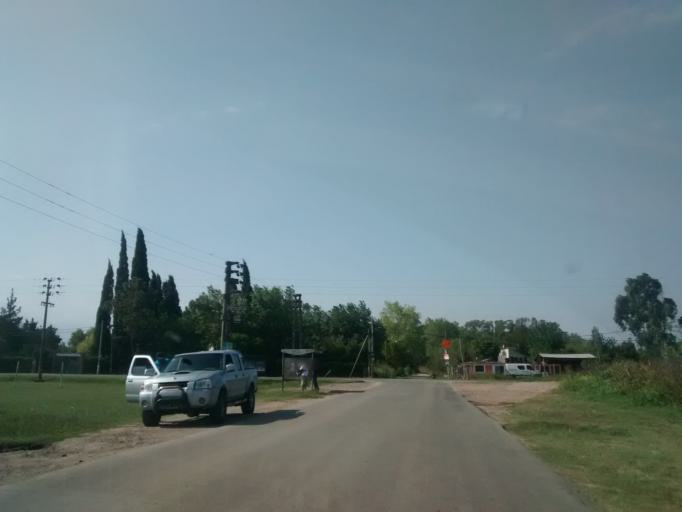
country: AR
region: Buenos Aires
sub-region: Partido de La Plata
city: La Plata
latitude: -34.9761
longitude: -57.8694
